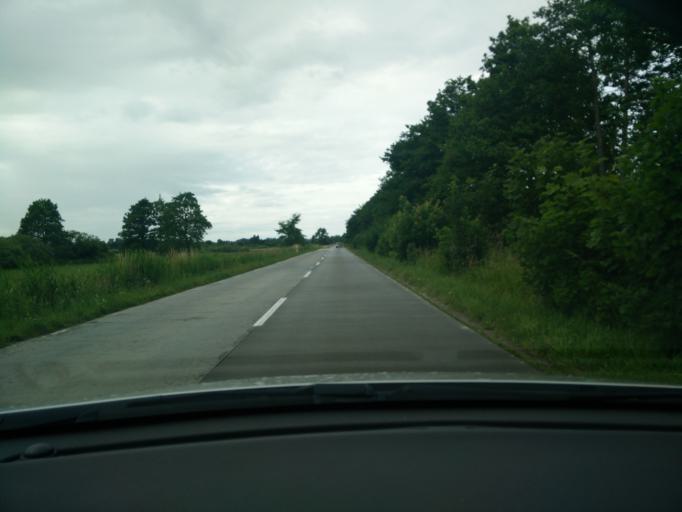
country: PL
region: Pomeranian Voivodeship
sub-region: Powiat pucki
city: Mrzezino
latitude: 54.6158
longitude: 18.4478
